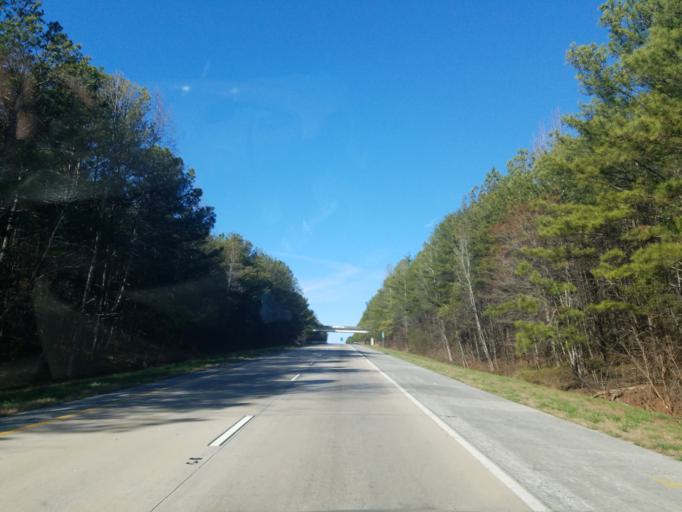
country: US
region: Georgia
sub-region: Cherokee County
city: Ball Ground
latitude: 34.3575
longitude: -84.3899
